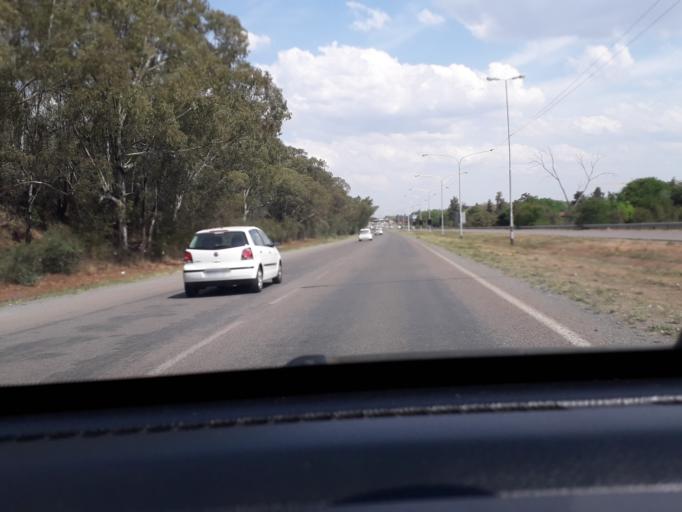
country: ZA
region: Gauteng
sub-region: City of Tshwane Metropolitan Municipality
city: Centurion
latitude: -25.8508
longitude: 28.2168
